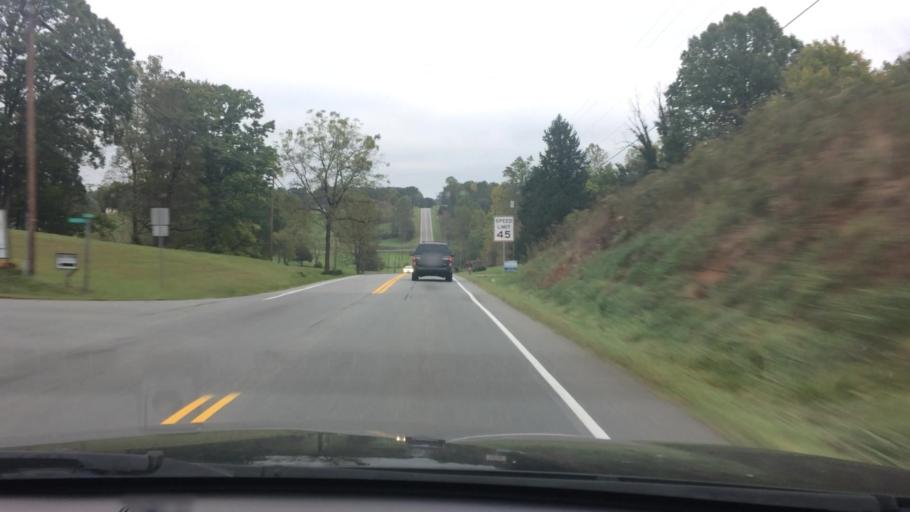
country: US
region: Virginia
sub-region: Franklin County
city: Rocky Mount
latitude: 37.0180
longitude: -79.8427
